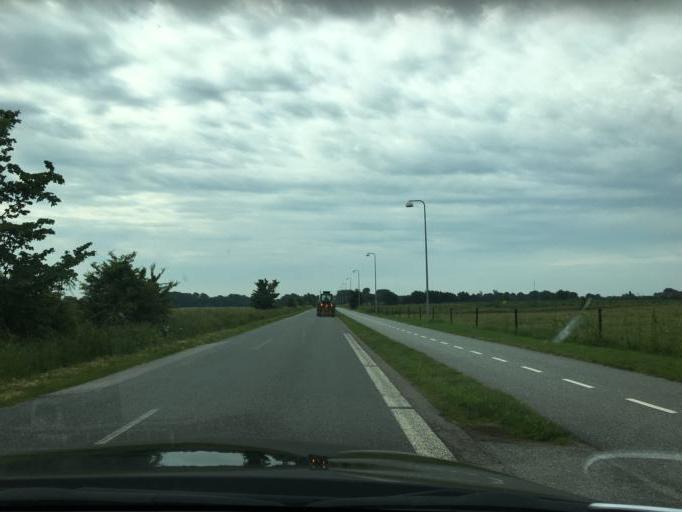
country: DK
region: South Denmark
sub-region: Kolding Kommune
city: Kolding
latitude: 55.5796
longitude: 9.4924
